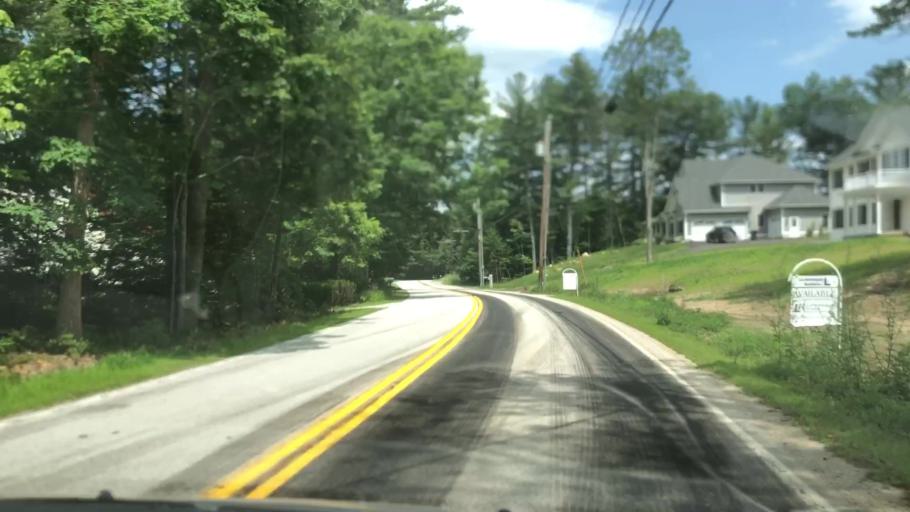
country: US
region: New Hampshire
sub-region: Hillsborough County
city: Bedford
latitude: 42.9383
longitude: -71.4918
